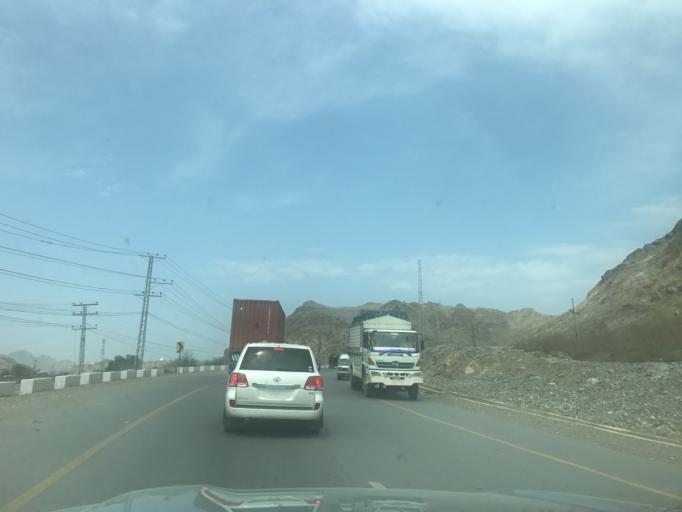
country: PK
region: Federally Administered Tribal Areas
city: Landi Kotal
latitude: 34.0858
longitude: 71.1692
